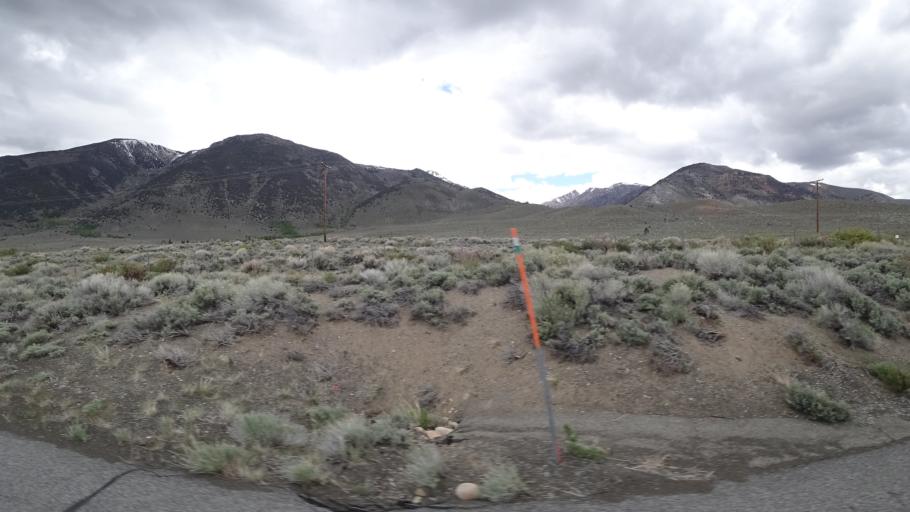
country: US
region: California
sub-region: Mono County
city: Bridgeport
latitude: 38.0277
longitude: -119.1557
